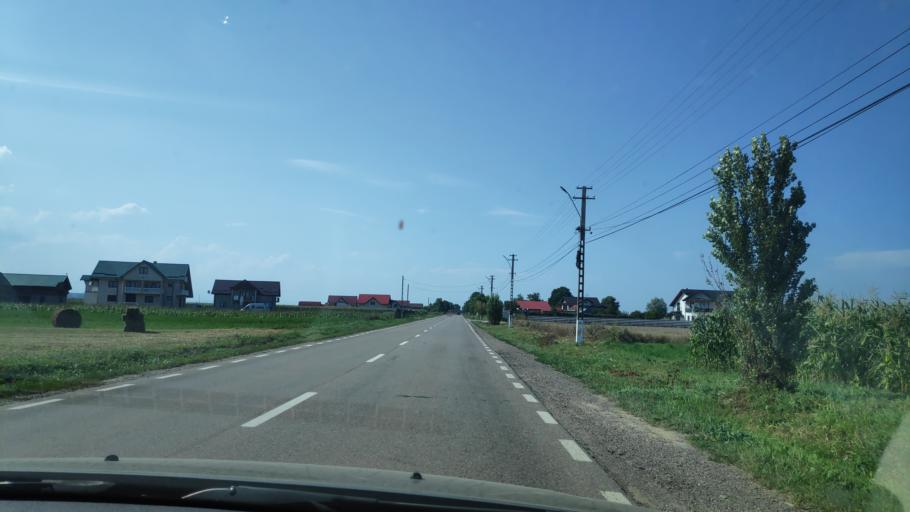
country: RO
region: Suceava
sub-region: Comuna Boroaia
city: Boroaia
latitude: 47.3658
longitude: 26.3350
